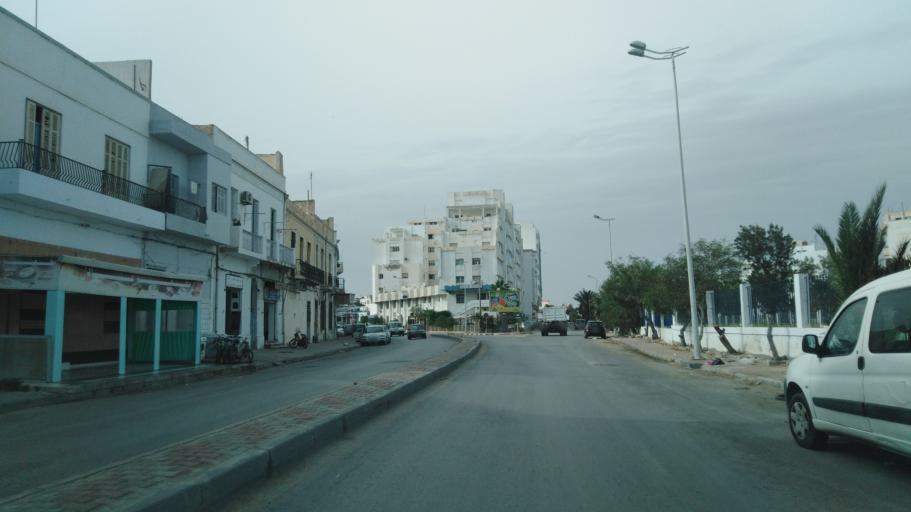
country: TN
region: Safaqis
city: Sfax
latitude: 34.7417
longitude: 10.7640
